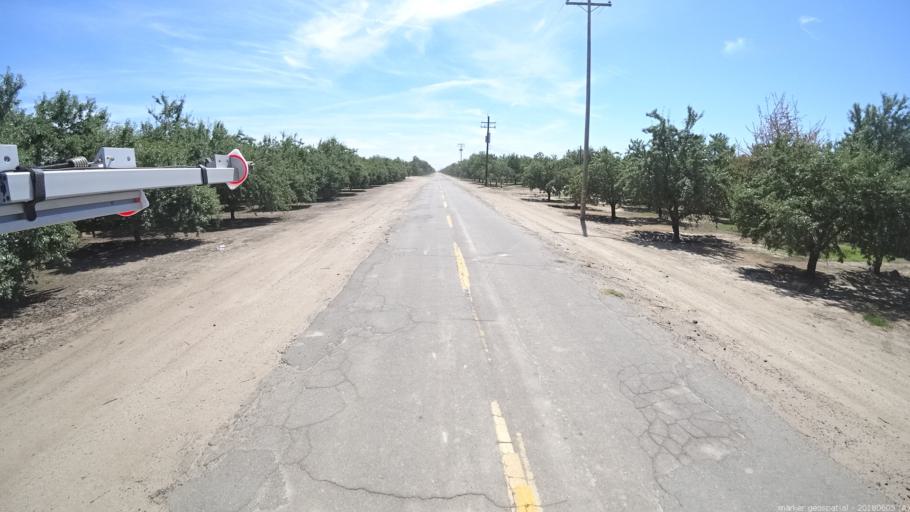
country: US
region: California
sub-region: Madera County
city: Chowchilla
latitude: 37.0982
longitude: -120.3975
